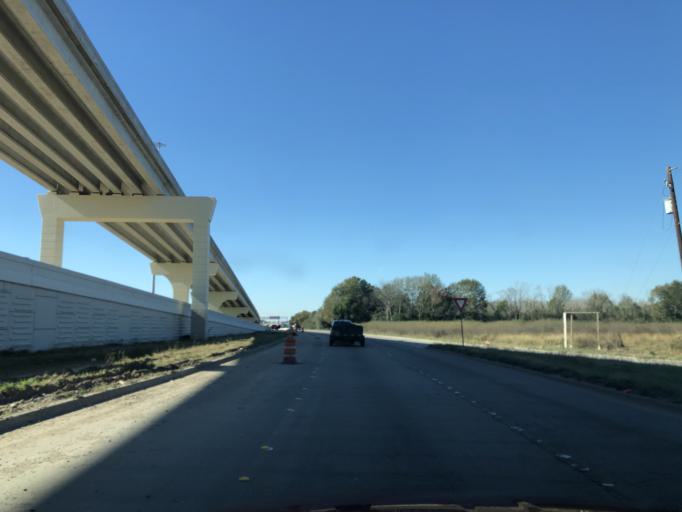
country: US
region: Texas
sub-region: Brazoria County
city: Brookside Village
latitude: 29.5978
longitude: -95.3903
